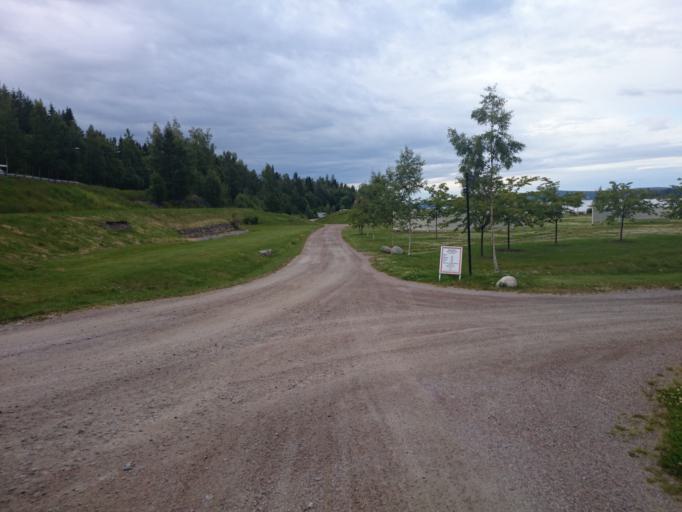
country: SE
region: Vaesternorrland
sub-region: Sundsvalls Kommun
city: Stockvik
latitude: 62.3195
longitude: 17.3695
